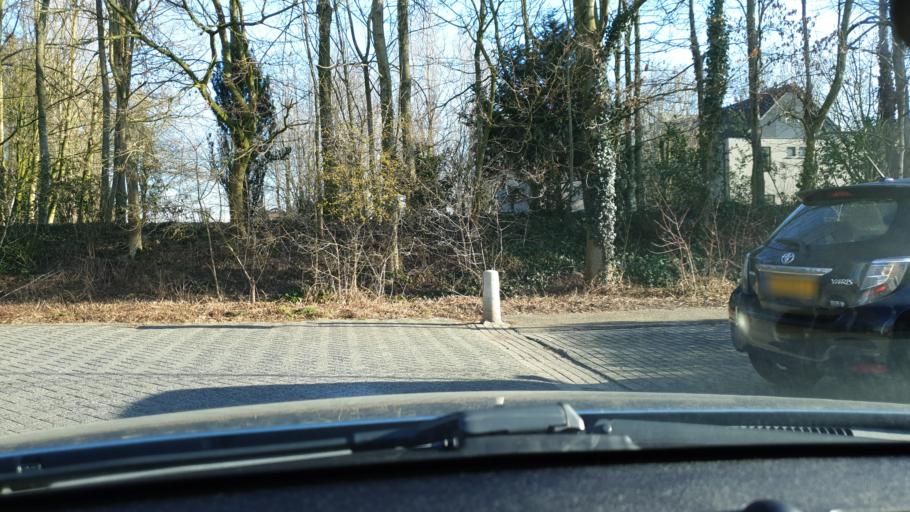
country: NL
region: Gelderland
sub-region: Gemeente Beuningen
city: Beuningen
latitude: 51.8649
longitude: 5.7692
